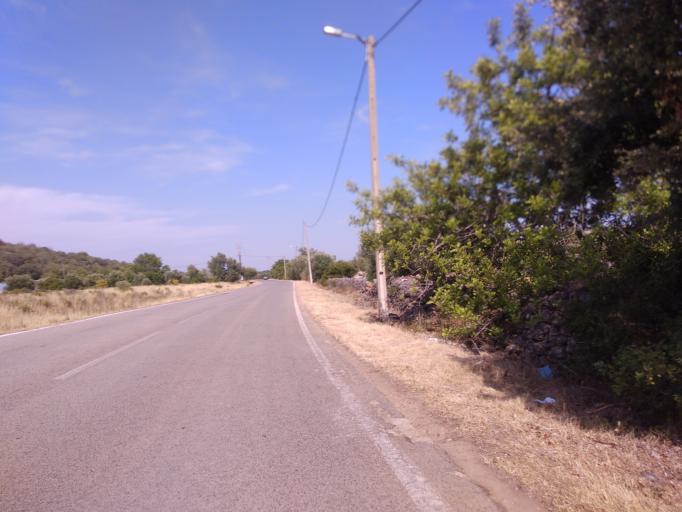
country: PT
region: Faro
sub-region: Sao Bras de Alportel
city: Sao Bras de Alportel
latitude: 37.1665
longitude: -7.9146
